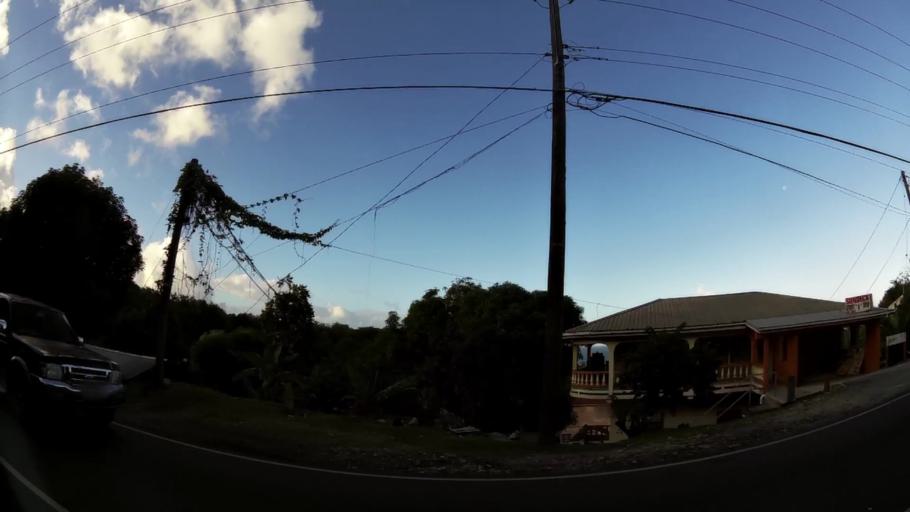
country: LC
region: Castries Quarter
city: Bisee
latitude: 14.0436
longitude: -60.9688
